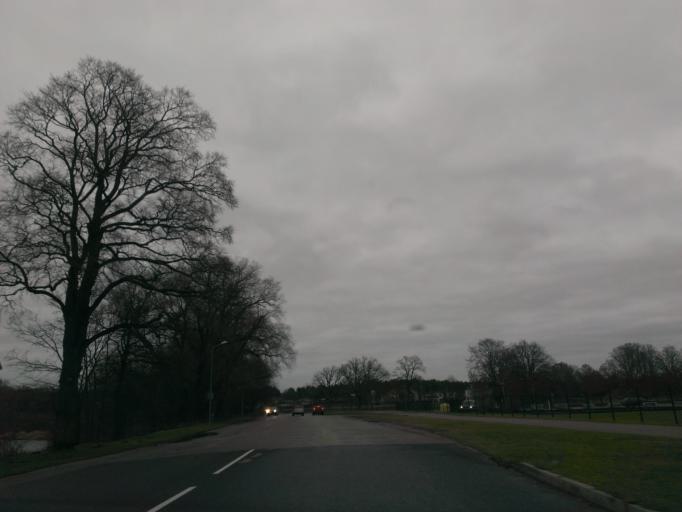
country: LV
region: Adazi
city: Adazi
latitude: 57.0798
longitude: 24.3390
